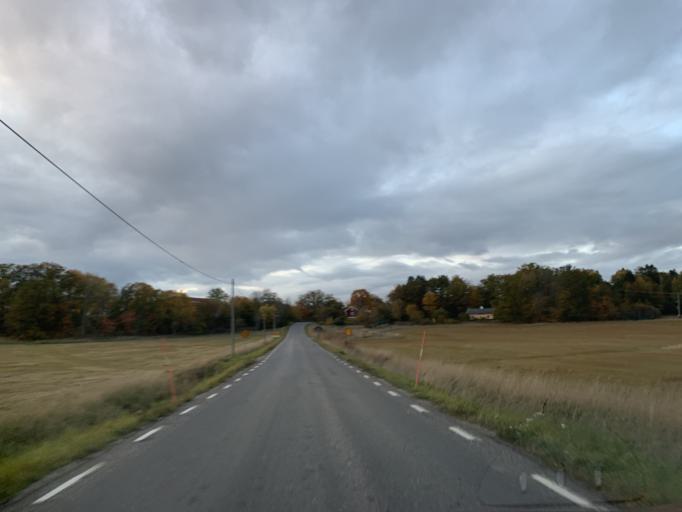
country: SE
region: Stockholm
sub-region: Nynashamns Kommun
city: Osmo
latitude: 58.9257
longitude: 17.7727
